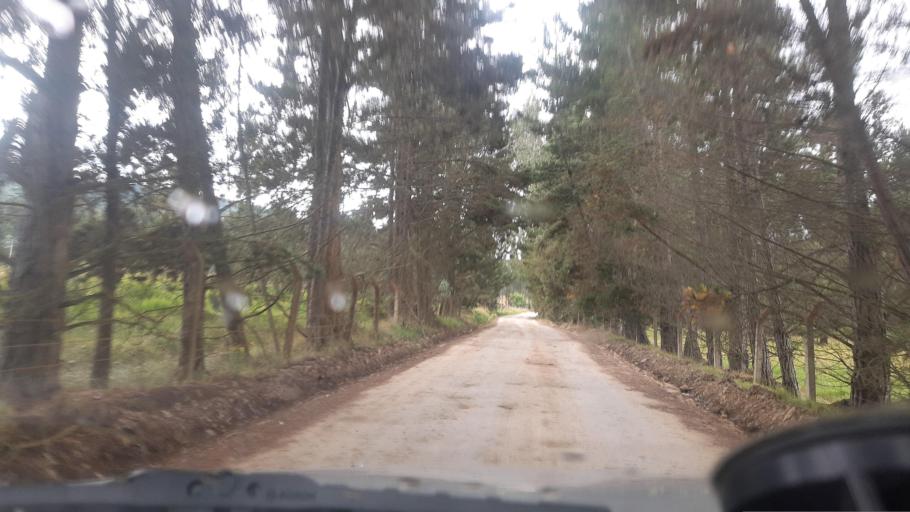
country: CO
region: Cundinamarca
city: Cucunuba
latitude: 5.1805
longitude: -73.8006
